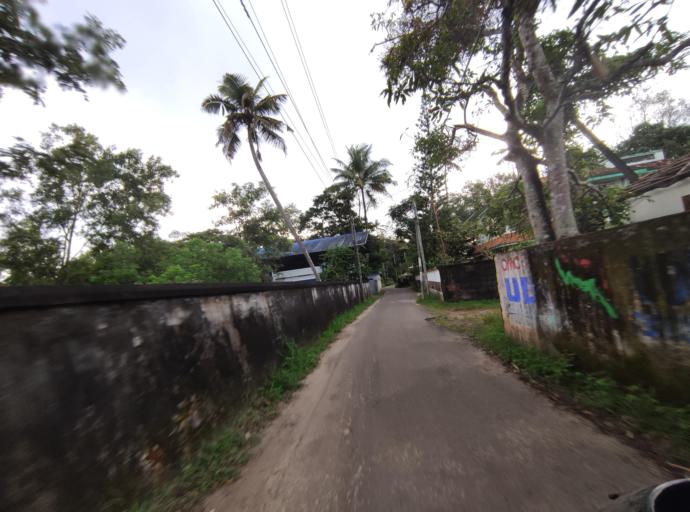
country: IN
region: Kerala
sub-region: Alappuzha
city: Shertallai
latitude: 9.6676
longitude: 76.3386
